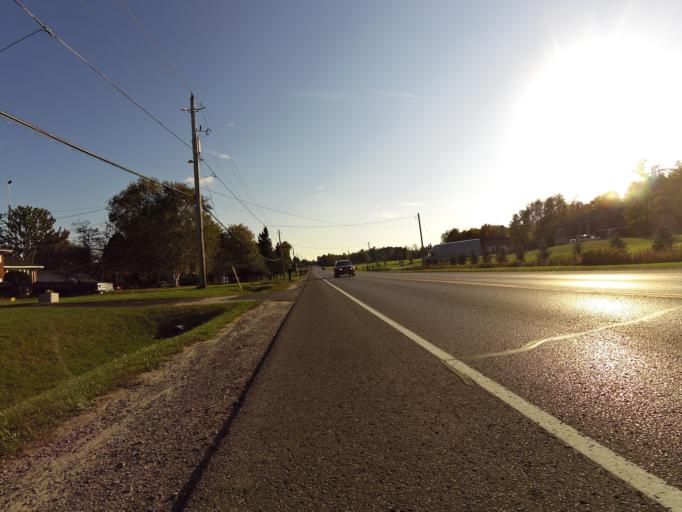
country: CA
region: Ontario
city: Kingston
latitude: 44.3202
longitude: -76.4621
